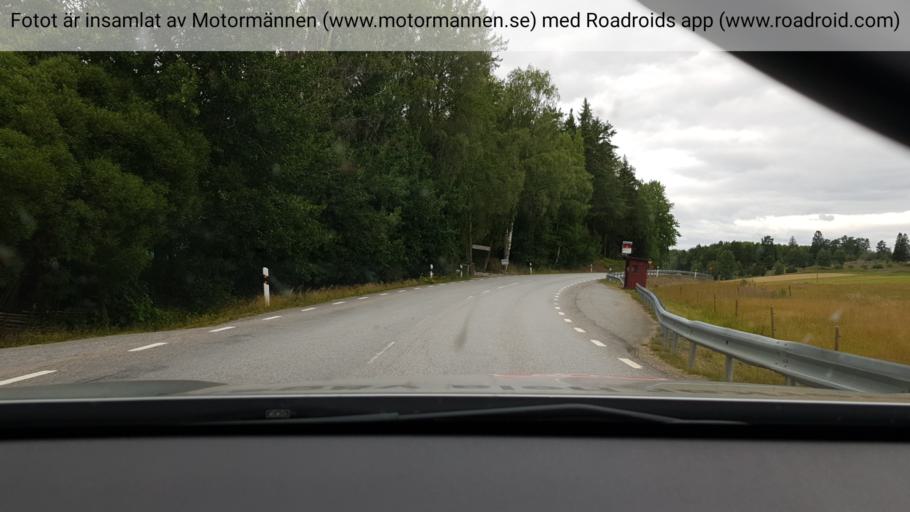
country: SE
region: Stockholm
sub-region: Nynashamns Kommun
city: Osmo
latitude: 58.9913
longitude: 17.8122
